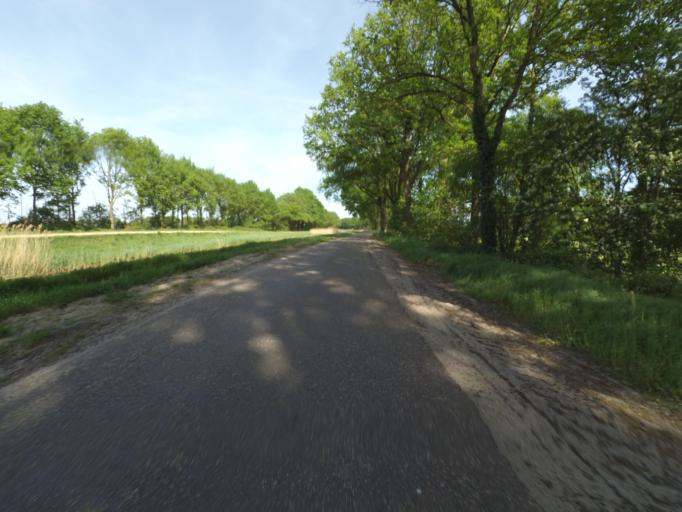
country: NL
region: Overijssel
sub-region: Gemeente Tubbergen
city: Tubbergen
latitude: 52.3655
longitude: 6.7845
